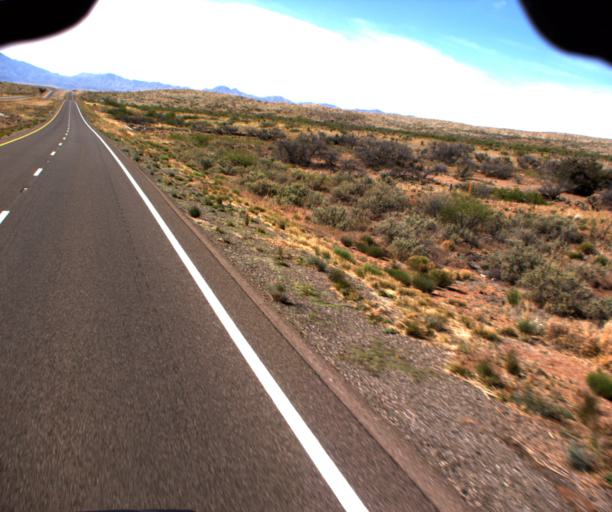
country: US
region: Arizona
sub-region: Cochise County
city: Willcox
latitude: 32.4400
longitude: -109.6640
